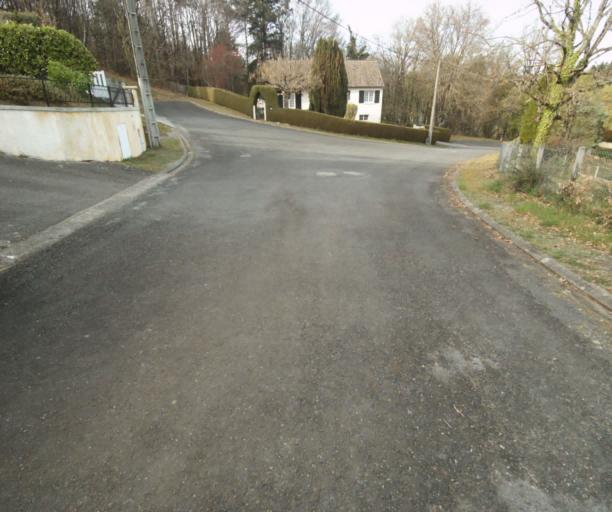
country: FR
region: Limousin
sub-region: Departement de la Correze
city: Naves
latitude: 45.3198
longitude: 1.7653
